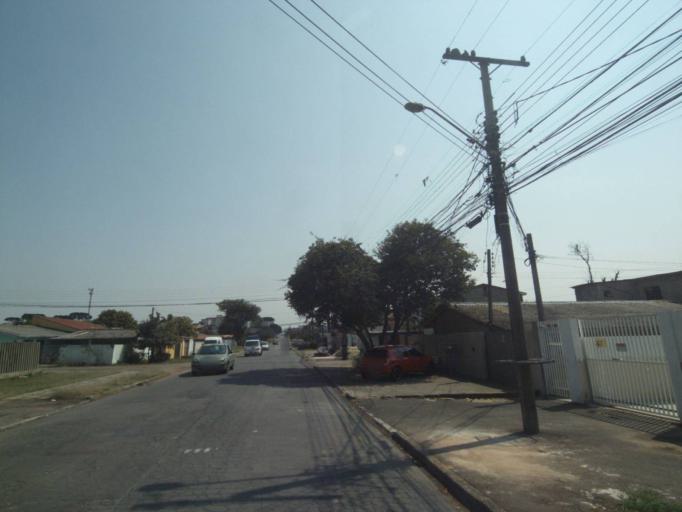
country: BR
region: Parana
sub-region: Sao Jose Dos Pinhais
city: Sao Jose dos Pinhais
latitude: -25.4905
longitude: -49.2512
